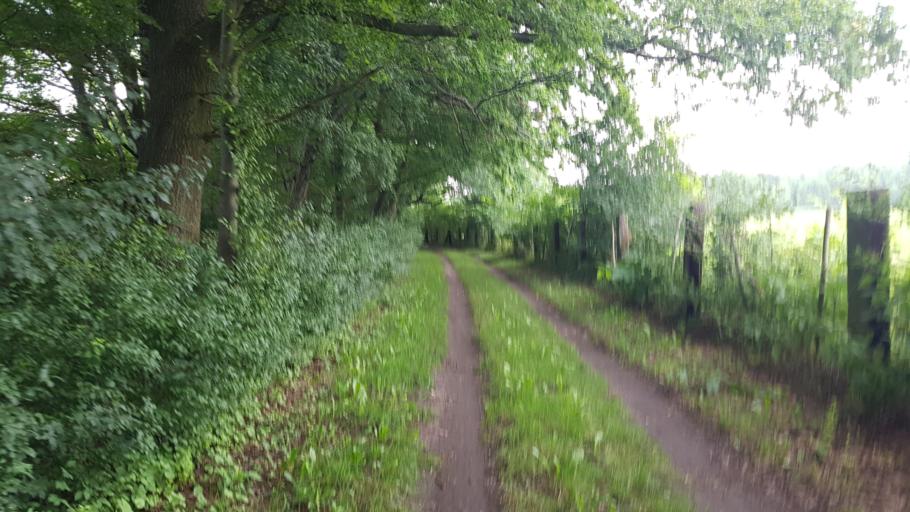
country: DE
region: Brandenburg
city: Sonnewalde
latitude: 51.6969
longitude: 13.6353
